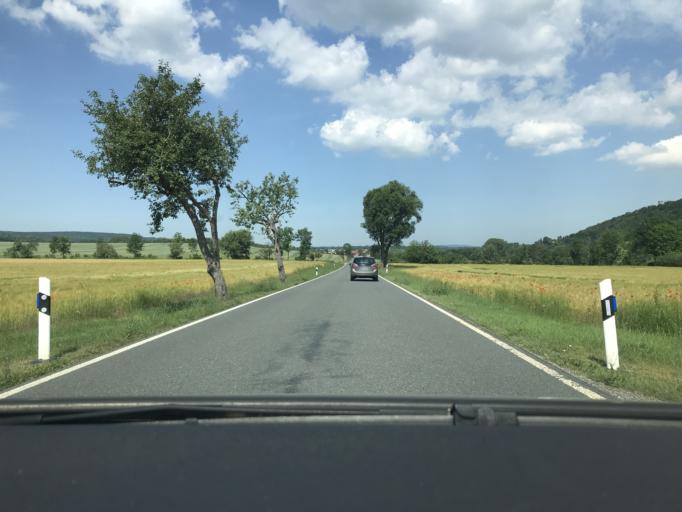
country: DE
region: Thuringia
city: Wandersleben
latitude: 50.8599
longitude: 10.8404
